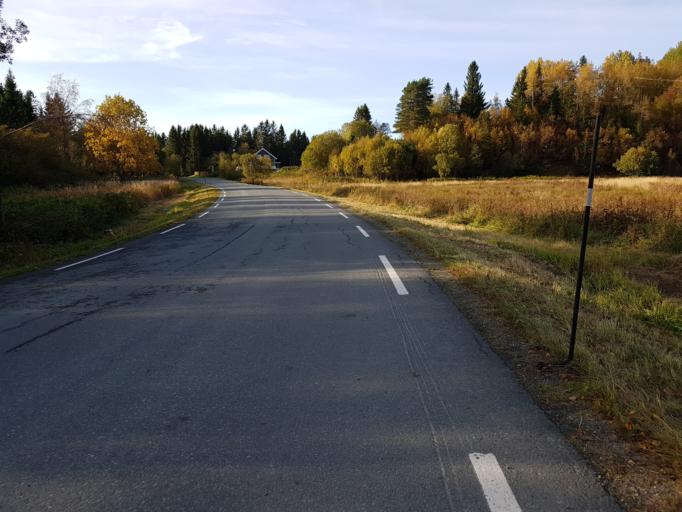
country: NO
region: Sor-Trondelag
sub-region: Klaebu
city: Klaebu
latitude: 63.3470
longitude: 10.5132
